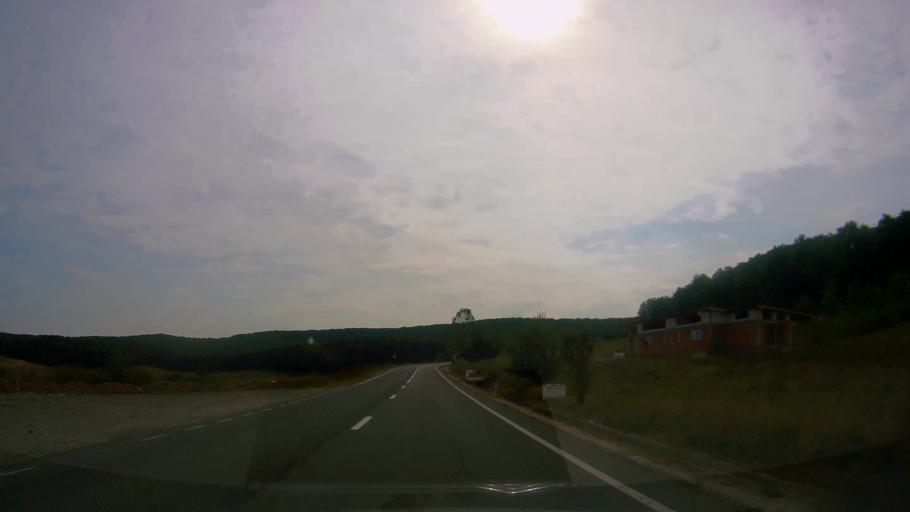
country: RO
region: Salaj
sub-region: Comuna Romanasi
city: Romanasi
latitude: 47.0781
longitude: 23.2018
